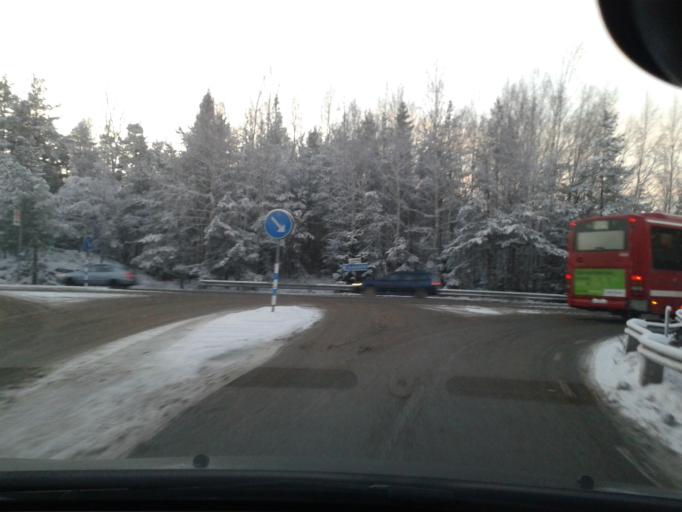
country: SE
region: Stockholm
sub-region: Haninge Kommun
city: Haninge
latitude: 59.1733
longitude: 18.1621
